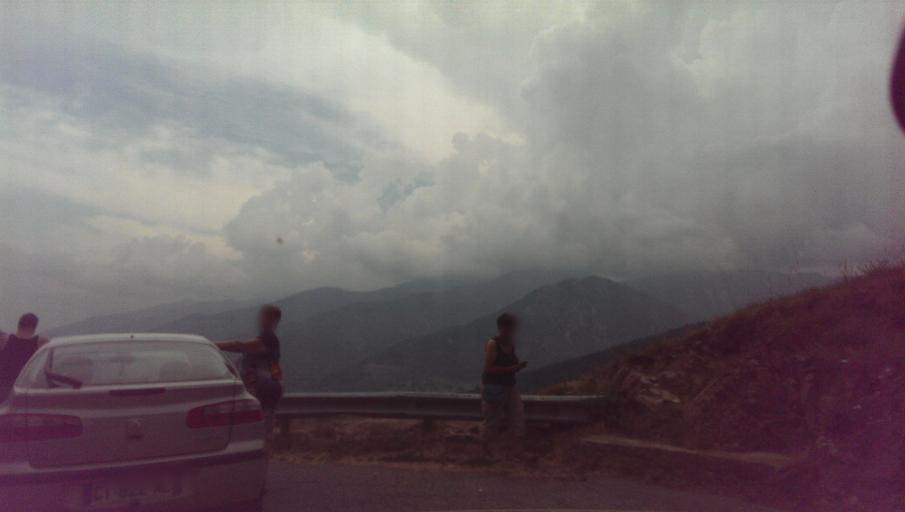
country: ES
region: Catalonia
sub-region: Provincia de Girona
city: Llivia
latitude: 42.5064
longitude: 2.1447
